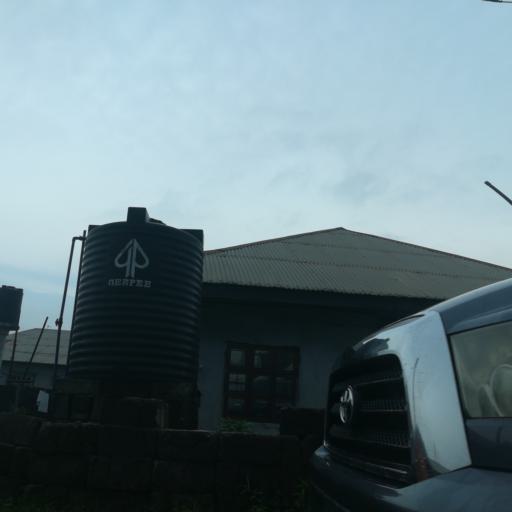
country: NG
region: Rivers
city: Port Harcourt
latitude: 4.7483
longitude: 7.0078
